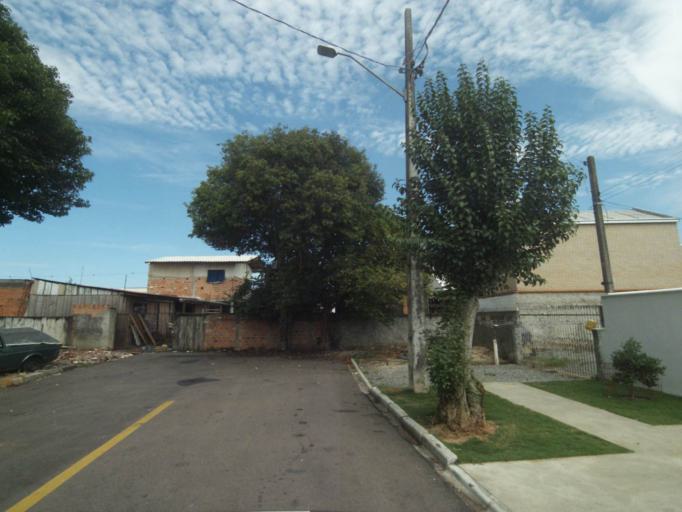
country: BR
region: Parana
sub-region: Pinhais
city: Pinhais
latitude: -25.4706
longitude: -49.1966
